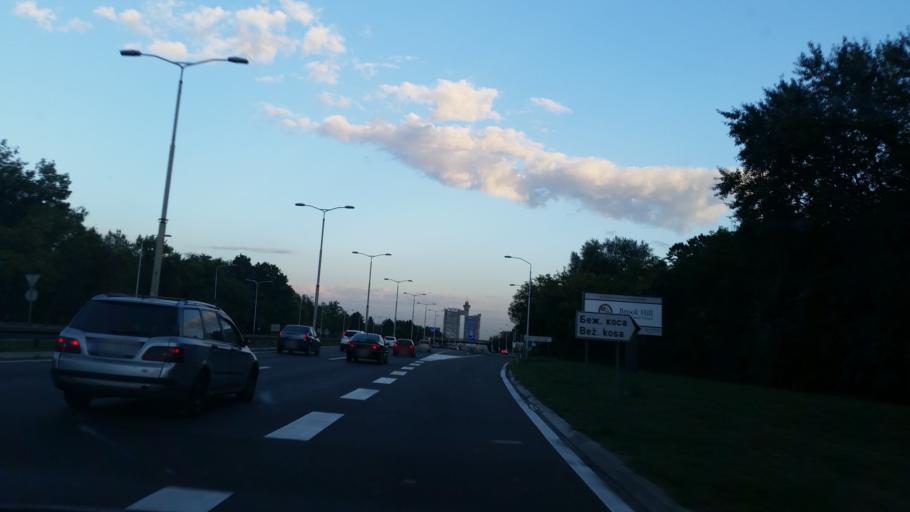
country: RS
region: Central Serbia
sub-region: Belgrade
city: Zemun
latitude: 44.8275
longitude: 20.3867
